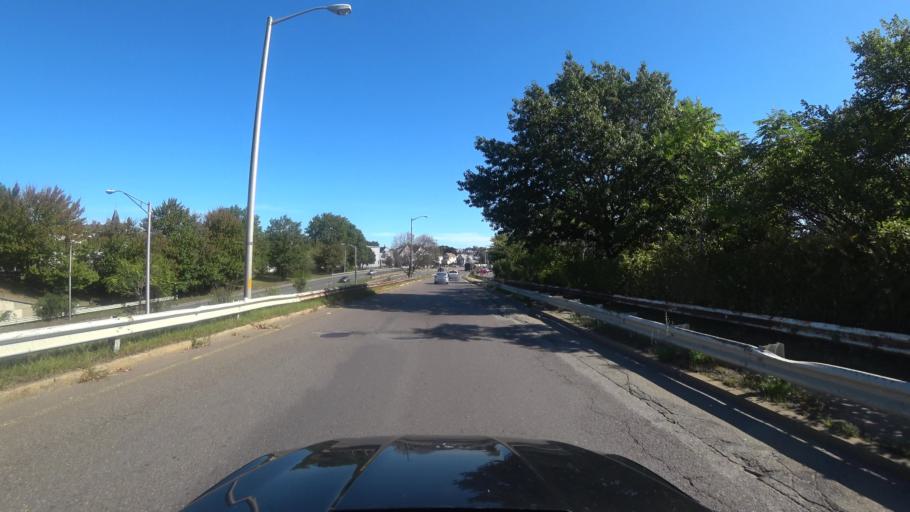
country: US
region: Massachusetts
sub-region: Middlesex County
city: Everett
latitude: 42.4022
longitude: -71.0597
